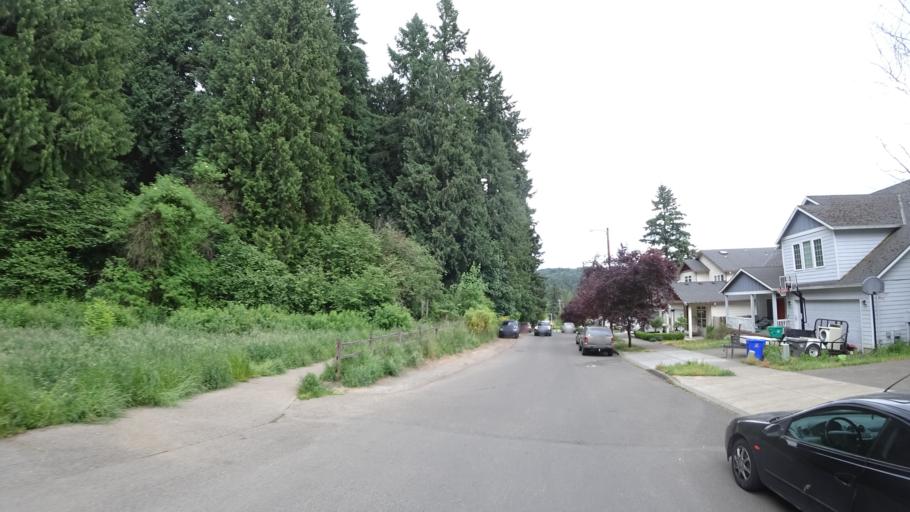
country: US
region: Oregon
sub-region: Clackamas County
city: Happy Valley
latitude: 45.4822
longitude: -122.5147
